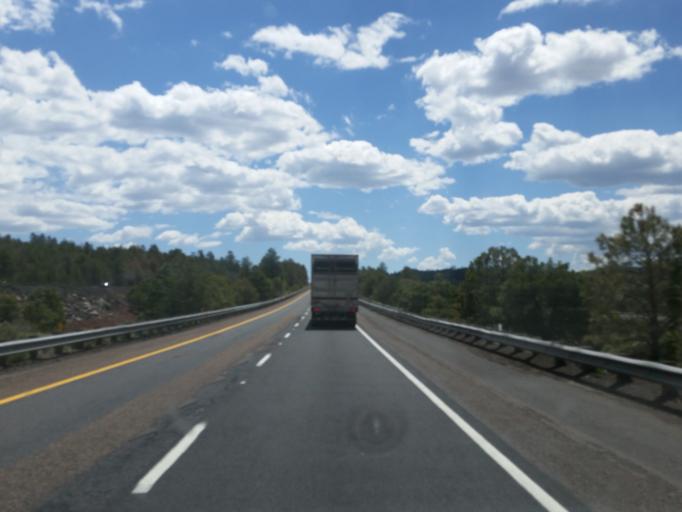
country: US
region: Arizona
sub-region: Coconino County
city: Parks
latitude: 35.2552
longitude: -111.9205
